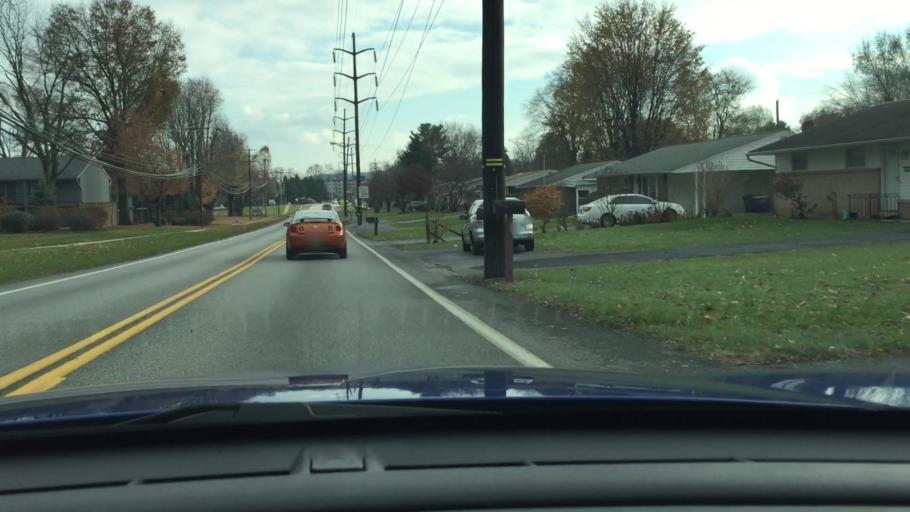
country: US
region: Pennsylvania
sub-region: Cumberland County
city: Shiremanstown
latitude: 40.2160
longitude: -76.9743
